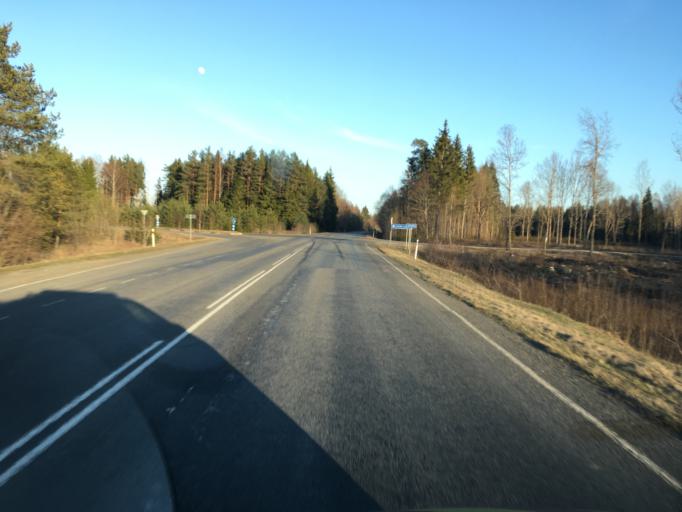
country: EE
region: Raplamaa
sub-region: Kehtna vald
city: Kehtna
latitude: 59.0653
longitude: 24.9262
